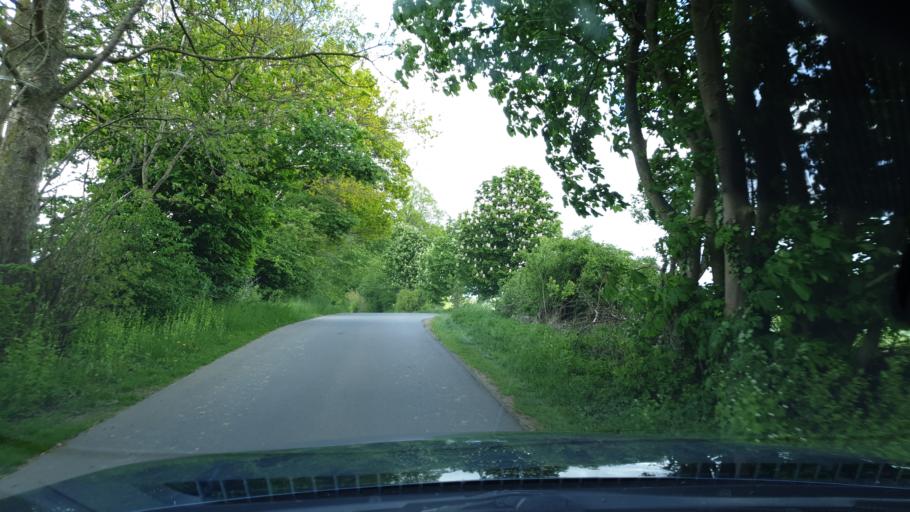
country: DE
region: Mecklenburg-Vorpommern
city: Bernitt
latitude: 53.9283
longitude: 11.8371
